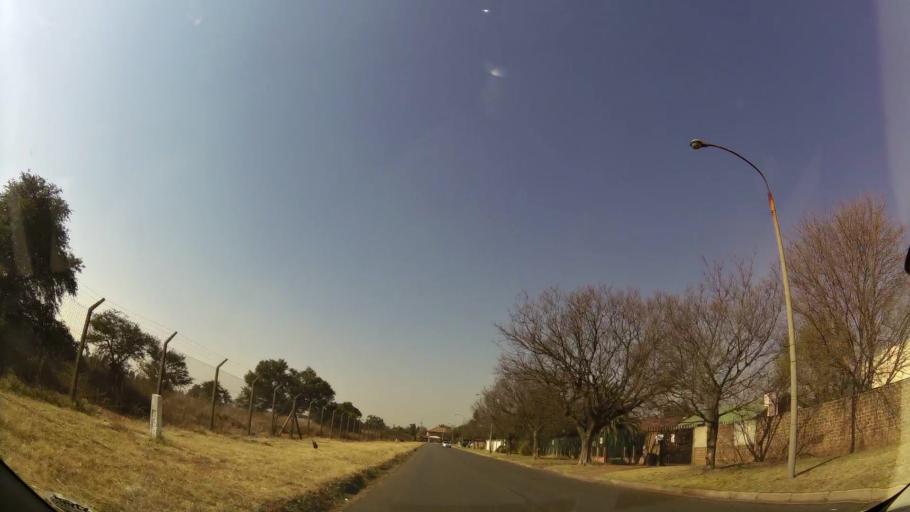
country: ZA
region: Gauteng
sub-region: Ekurhuleni Metropolitan Municipality
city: Boksburg
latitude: -26.1565
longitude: 28.2623
